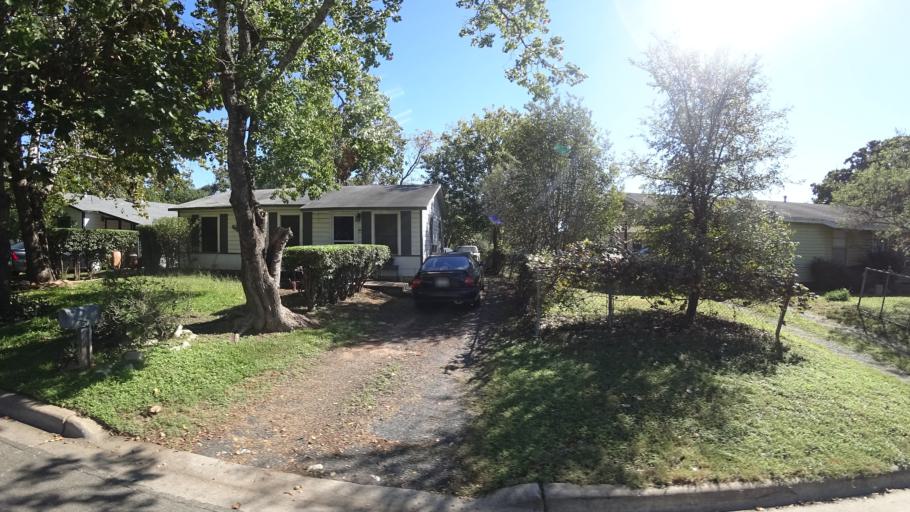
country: US
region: Texas
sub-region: Travis County
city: Austin
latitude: 30.2817
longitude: -97.6868
